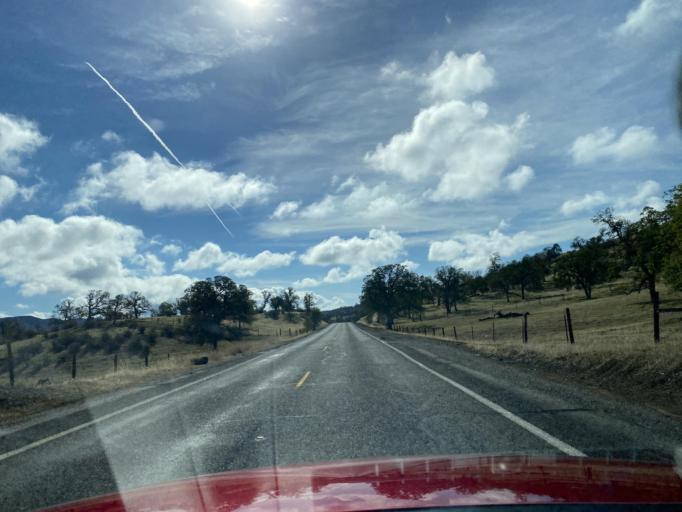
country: US
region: California
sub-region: Glenn County
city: Willows
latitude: 39.5093
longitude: -122.5266
